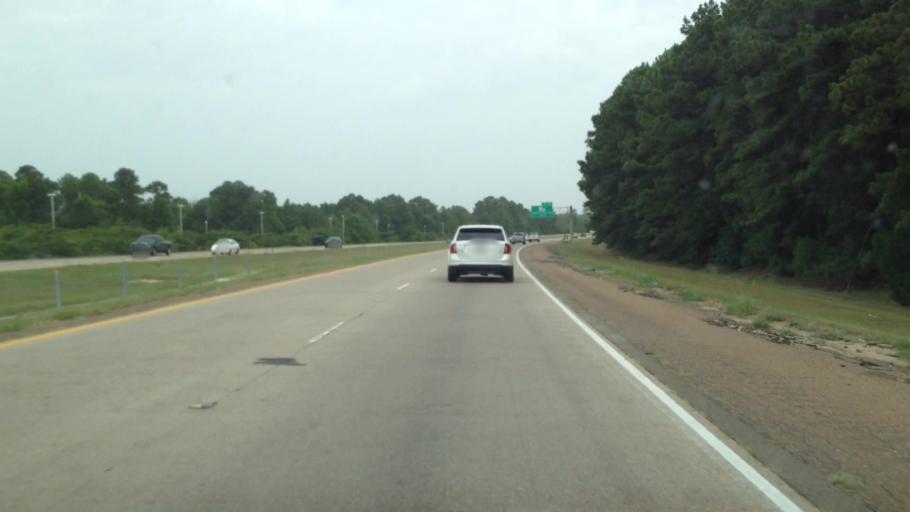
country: US
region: Louisiana
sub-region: Caddo Parish
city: Shreveport
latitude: 32.4235
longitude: -93.8360
